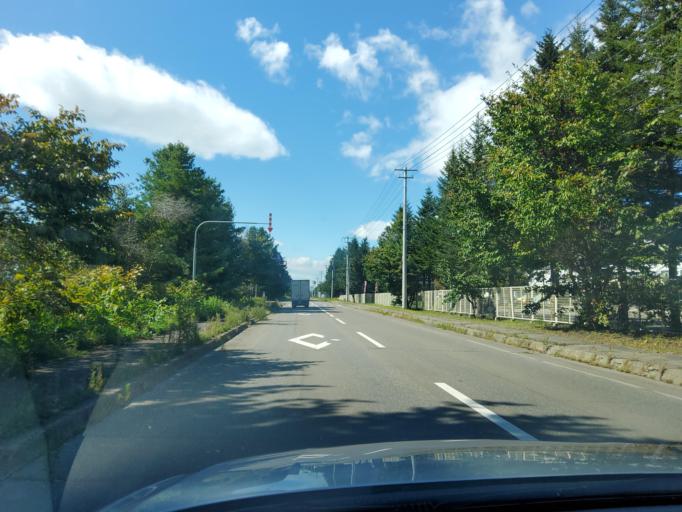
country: JP
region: Hokkaido
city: Obihiro
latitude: 42.9366
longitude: 143.2898
